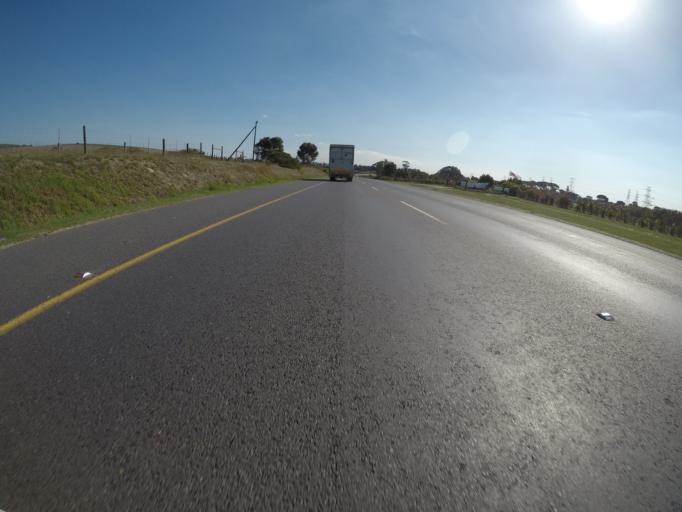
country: ZA
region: Western Cape
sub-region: City of Cape Town
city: Kraaifontein
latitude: -33.9017
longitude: 18.7241
